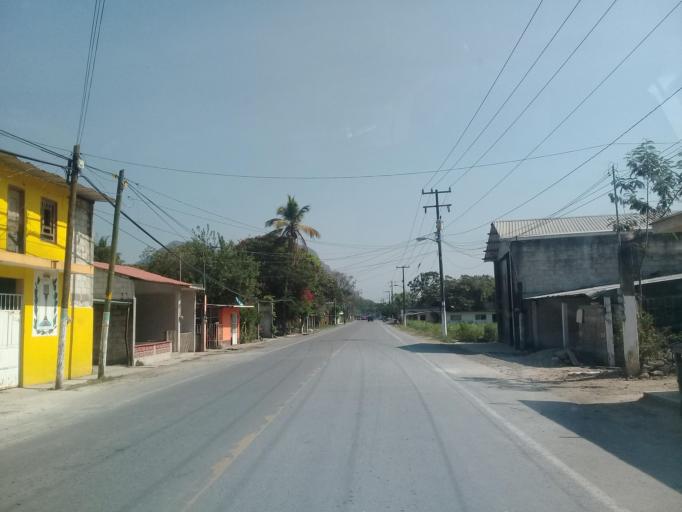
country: MX
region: Veracruz
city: Rafael Delgado
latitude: 18.7872
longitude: -97.0107
